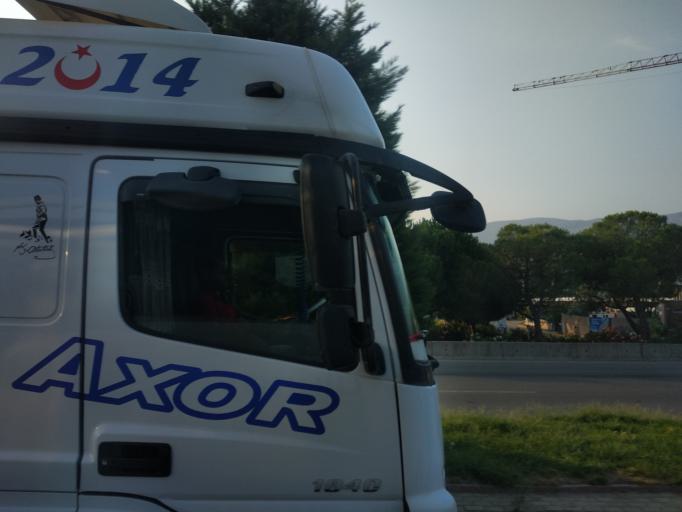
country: TR
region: Manisa
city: Salihli
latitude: 38.4835
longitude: 28.1227
